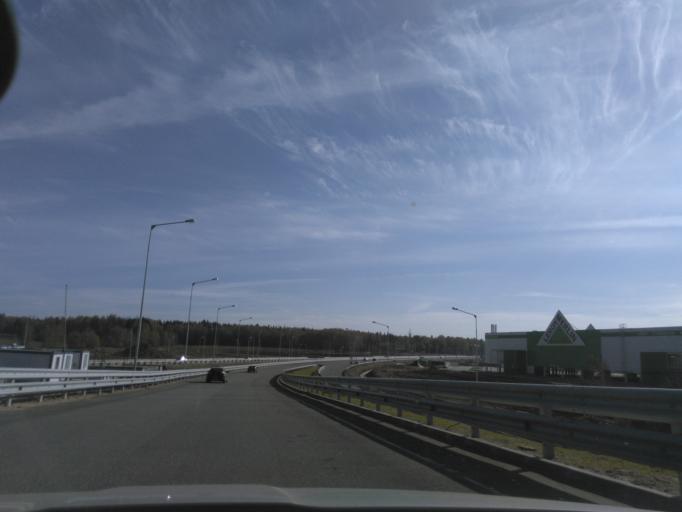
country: RU
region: Moskovskaya
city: Rzhavki
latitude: 56.0008
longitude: 37.2491
